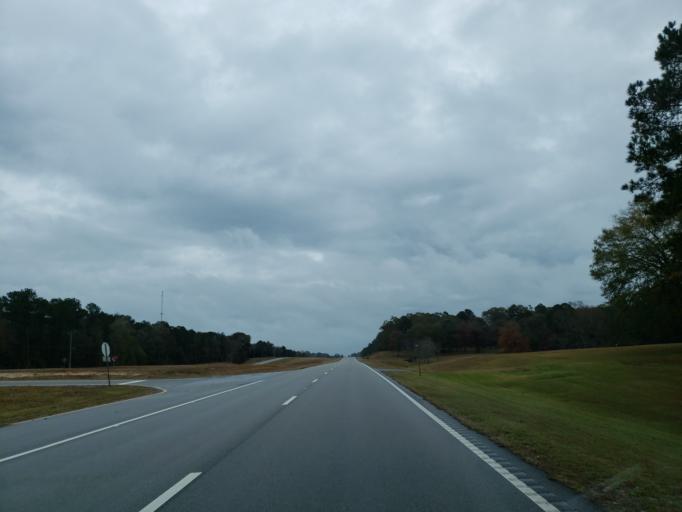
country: US
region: Mississippi
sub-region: Wayne County
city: Waynesboro
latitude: 31.6953
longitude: -88.7481
